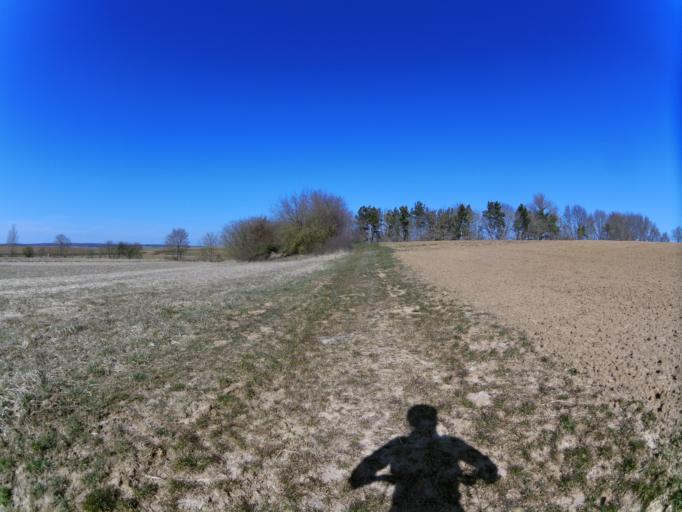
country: DE
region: Bavaria
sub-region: Regierungsbezirk Unterfranken
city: Oberpleichfeld
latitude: 49.8736
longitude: 10.0702
